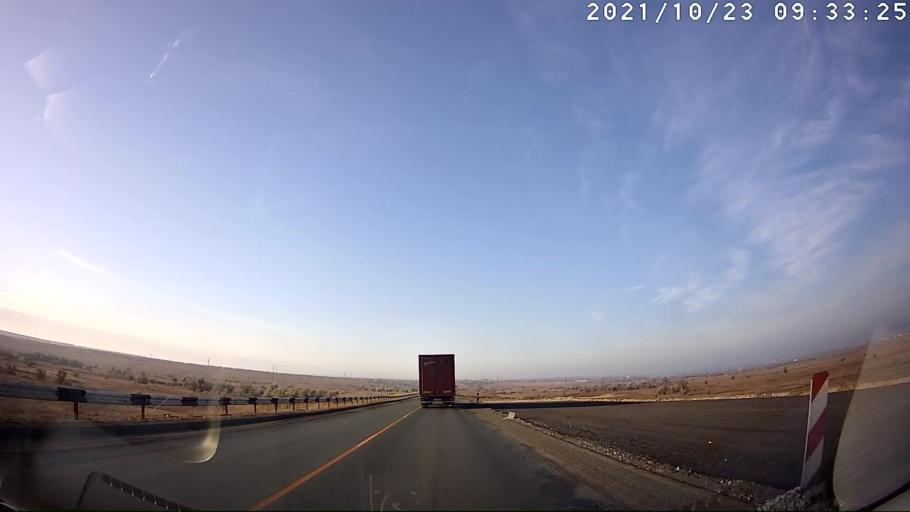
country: RU
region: Saratov
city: Sokolovyy
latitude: 51.6627
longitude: 45.8503
